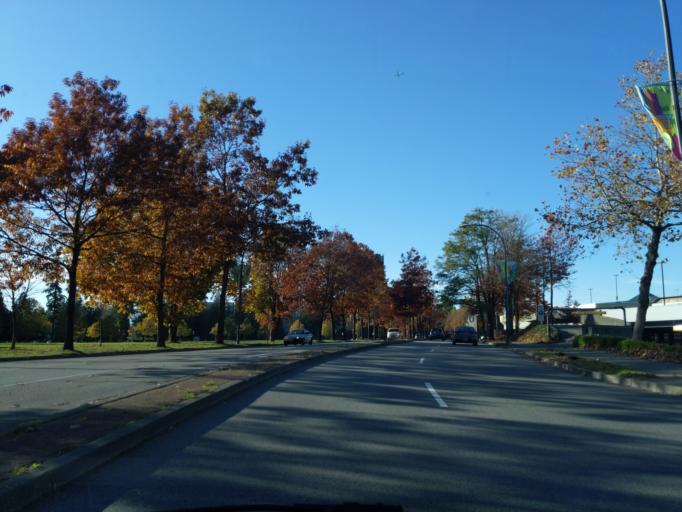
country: CA
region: British Columbia
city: New Westminster
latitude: 49.1844
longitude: -122.8474
